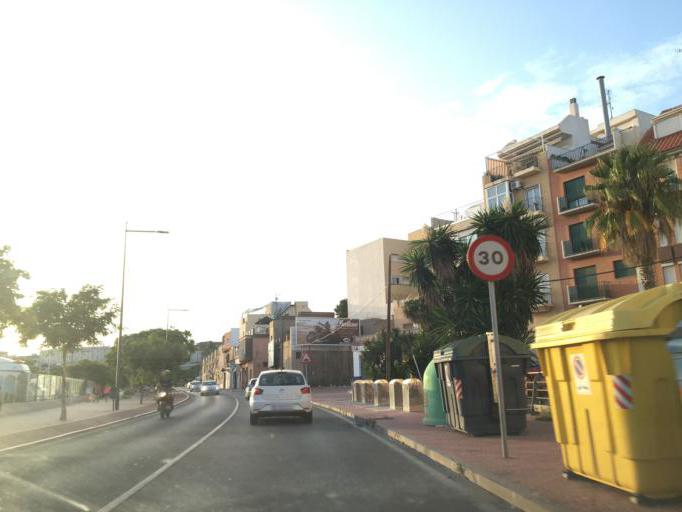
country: ES
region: Murcia
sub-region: Murcia
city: Cartagena
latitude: 37.5983
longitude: -0.9736
